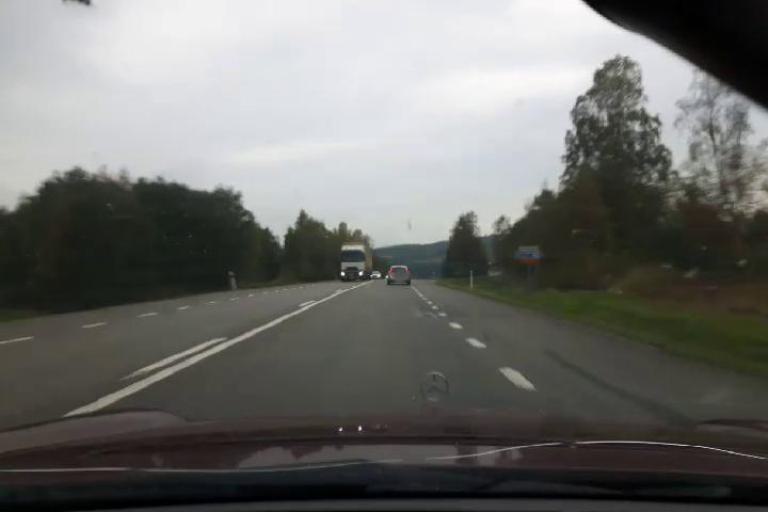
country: SE
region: Vaesternorrland
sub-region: Kramfors Kommun
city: Nordingra
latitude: 63.0280
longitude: 18.3035
